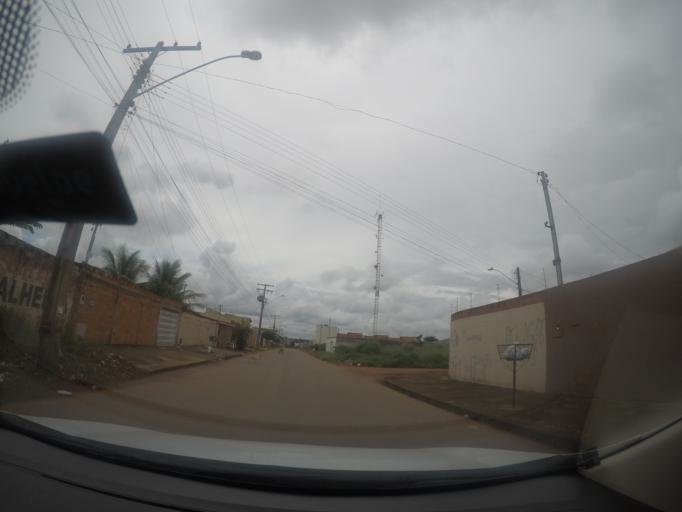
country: BR
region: Goias
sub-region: Trindade
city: Trindade
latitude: -16.6908
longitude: -49.4050
